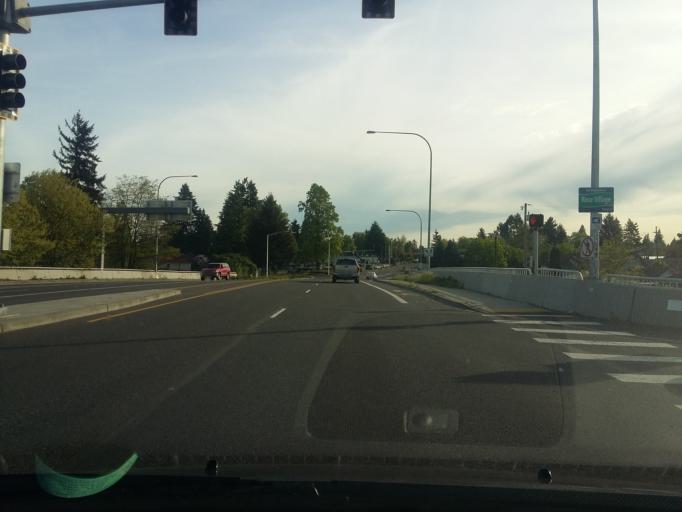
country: US
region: Washington
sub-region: Clark County
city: Minnehaha
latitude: 45.6466
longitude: -122.6423
